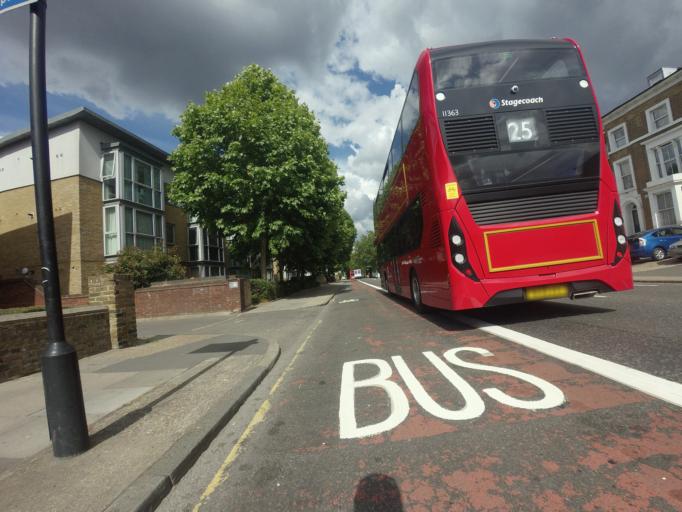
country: GB
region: England
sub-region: Greater London
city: East Ham
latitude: 51.5452
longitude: 0.0181
